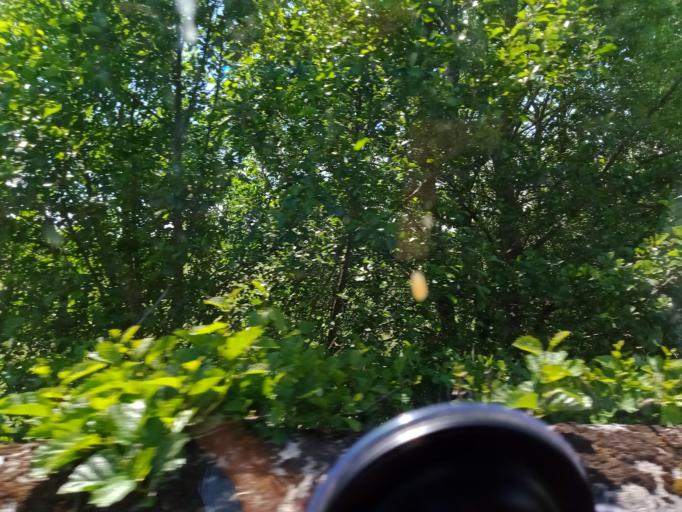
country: IE
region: Leinster
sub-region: Kilkenny
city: Thomastown
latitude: 52.5499
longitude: -7.0785
